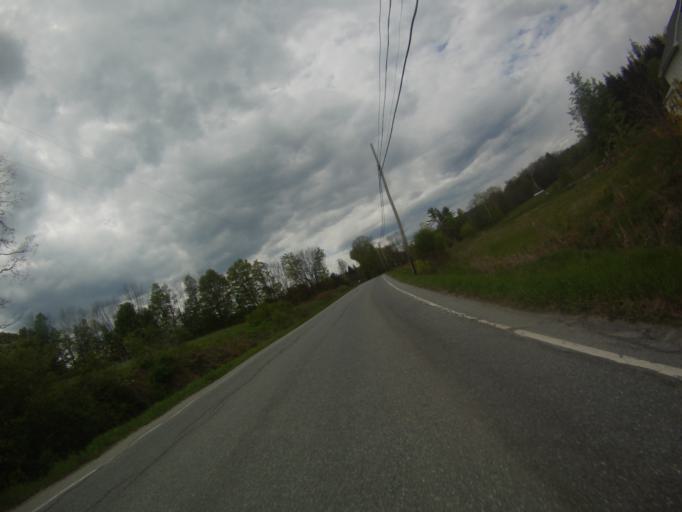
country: US
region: New York
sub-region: Essex County
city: Port Henry
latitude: 43.9509
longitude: -73.4792
